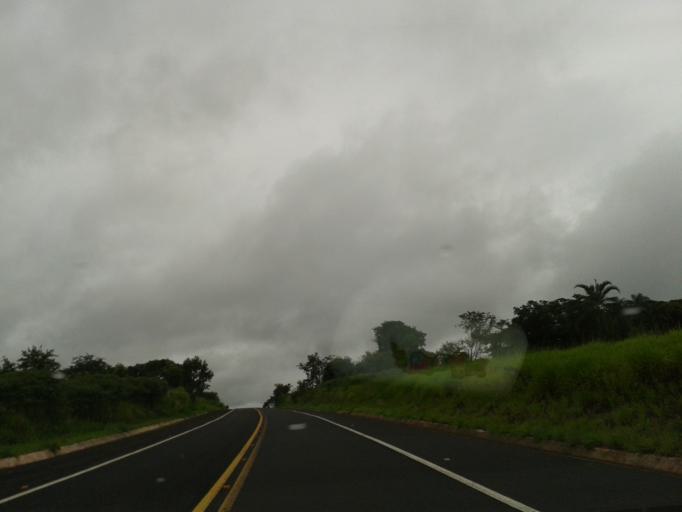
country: BR
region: Minas Gerais
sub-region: Santa Vitoria
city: Santa Vitoria
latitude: -19.2087
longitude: -50.0231
